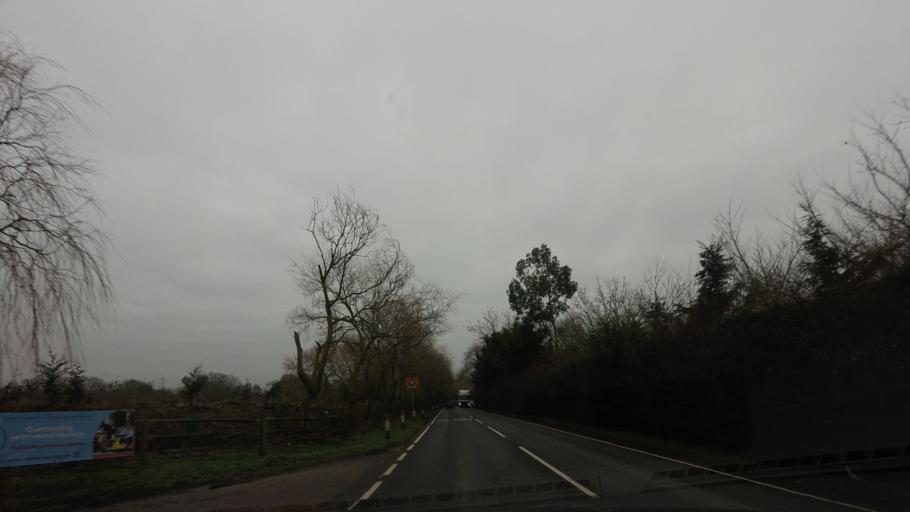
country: GB
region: England
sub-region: Kent
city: Staplehurst
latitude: 51.1911
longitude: 0.5420
